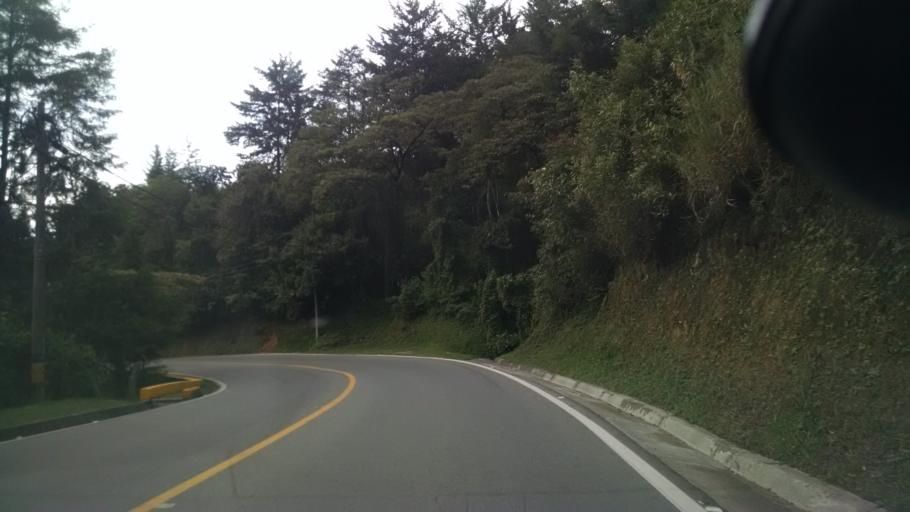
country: CO
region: Antioquia
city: El Retiro
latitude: 6.0866
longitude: -75.4785
